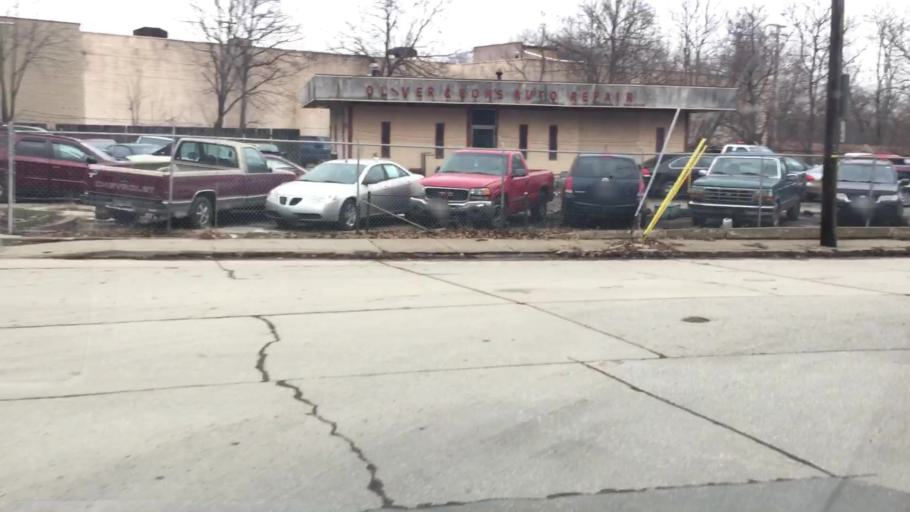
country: US
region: Ohio
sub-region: Summit County
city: Akron
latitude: 41.0788
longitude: -81.4904
